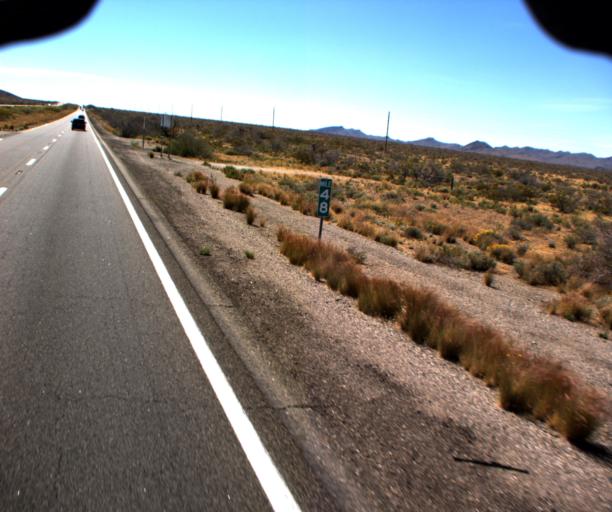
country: US
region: Arizona
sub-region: Mohave County
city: Dolan Springs
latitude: 35.4564
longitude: -114.3020
